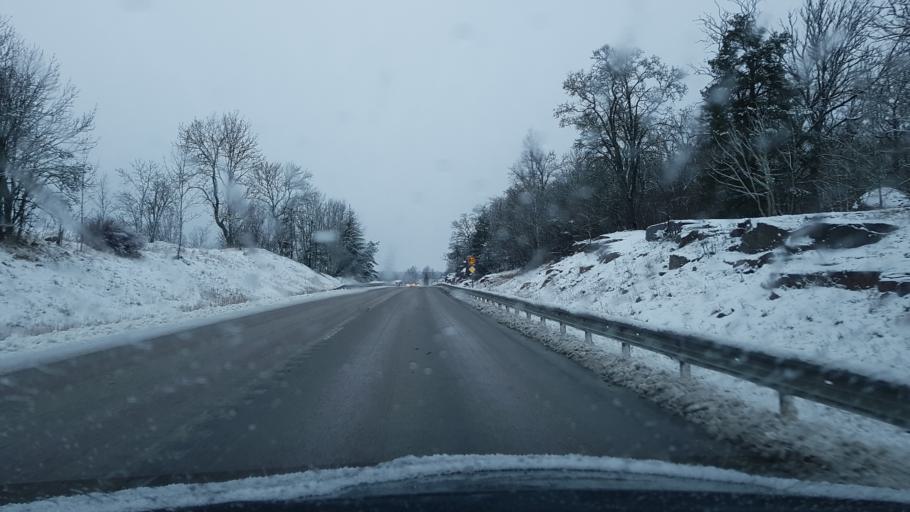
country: SE
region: Uppsala
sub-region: Enkopings Kommun
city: Orsundsbro
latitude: 59.8752
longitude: 17.2918
